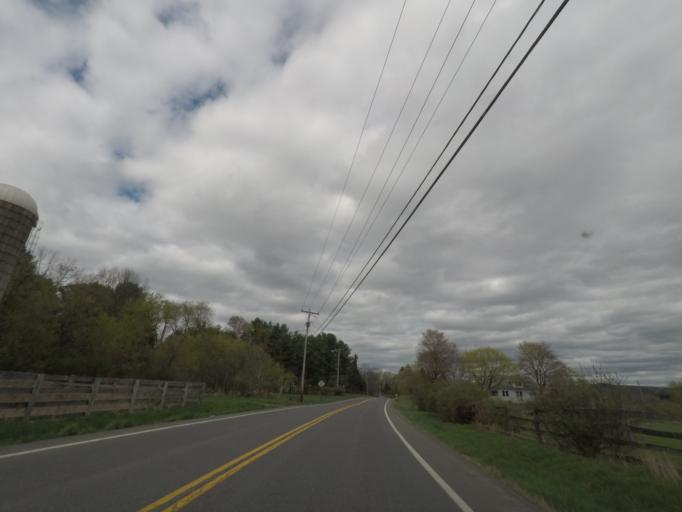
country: US
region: New York
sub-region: Columbia County
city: Philmont
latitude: 42.2789
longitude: -73.6599
